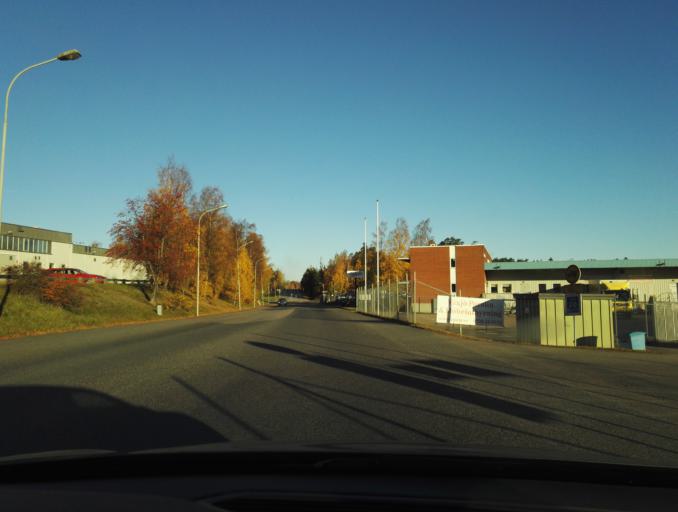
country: SE
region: Kronoberg
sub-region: Vaxjo Kommun
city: Vaexjoe
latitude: 56.8896
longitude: 14.7708
